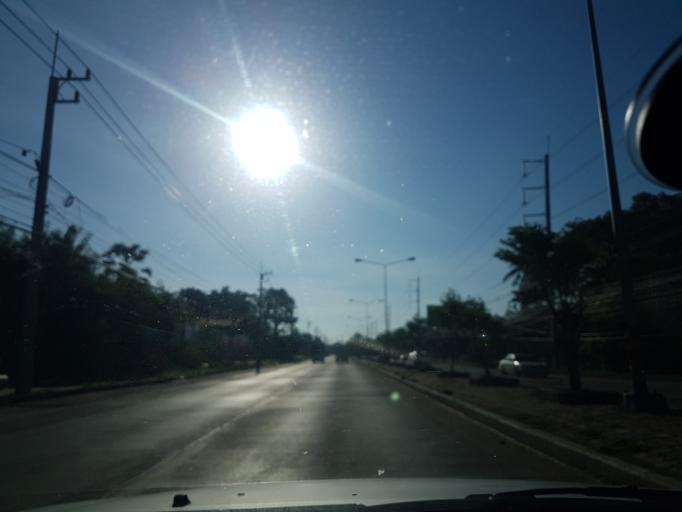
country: TH
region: Lop Buri
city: Lop Buri
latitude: 14.7730
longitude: 100.6995
